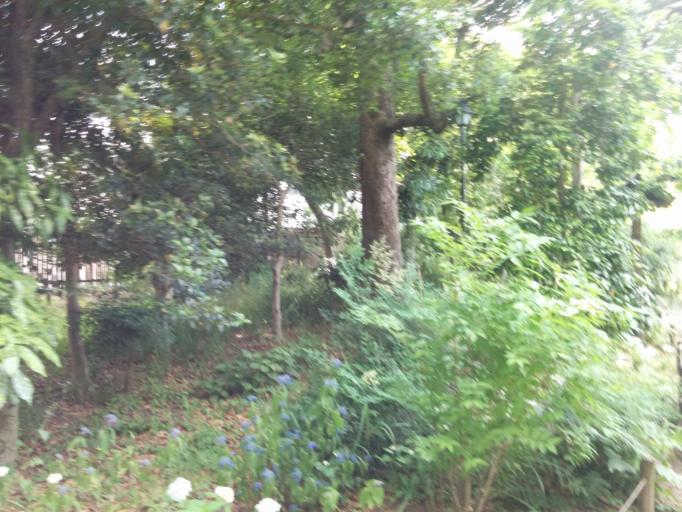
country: JP
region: Tokyo
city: Urayasu
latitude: 35.7240
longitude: 139.8161
